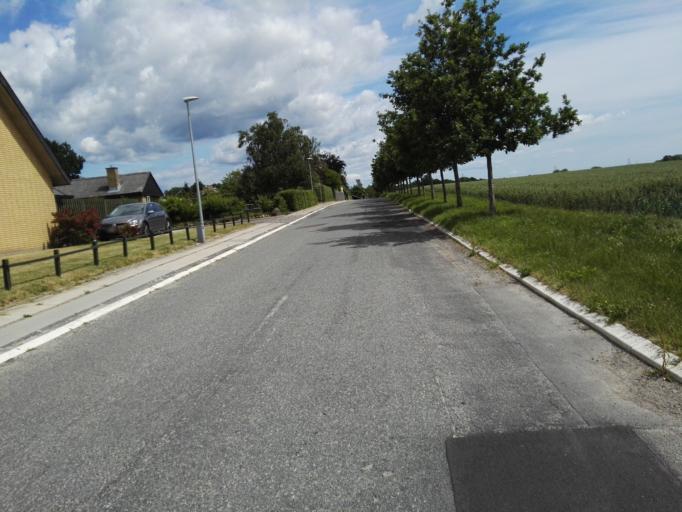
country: DK
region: Capital Region
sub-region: Egedal Kommune
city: Stenlose
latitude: 55.7586
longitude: 12.1924
